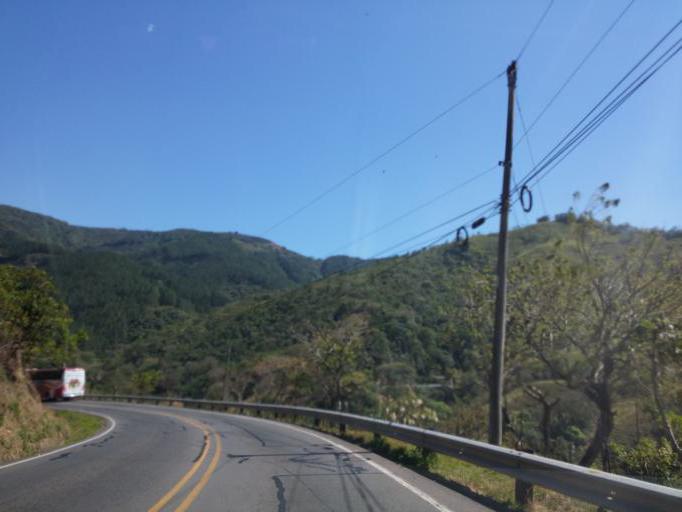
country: CR
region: Heredia
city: Colon
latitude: 9.8869
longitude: -84.2263
